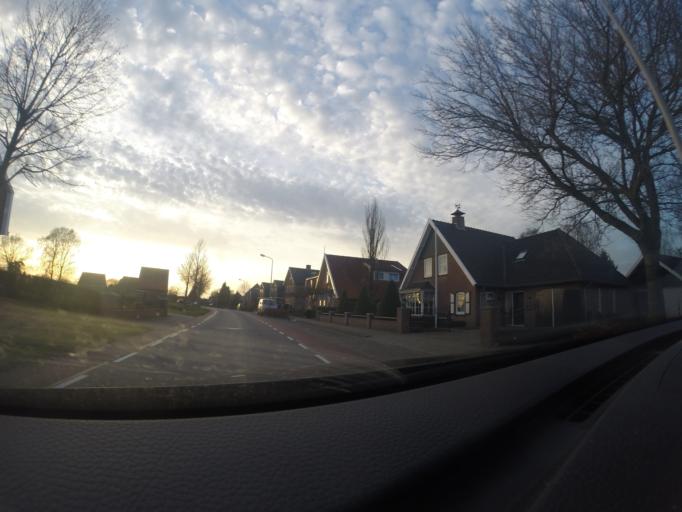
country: NL
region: Overijssel
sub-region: Gemeente Haaksbergen
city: Haaksbergen
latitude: 52.1540
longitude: 6.7591
